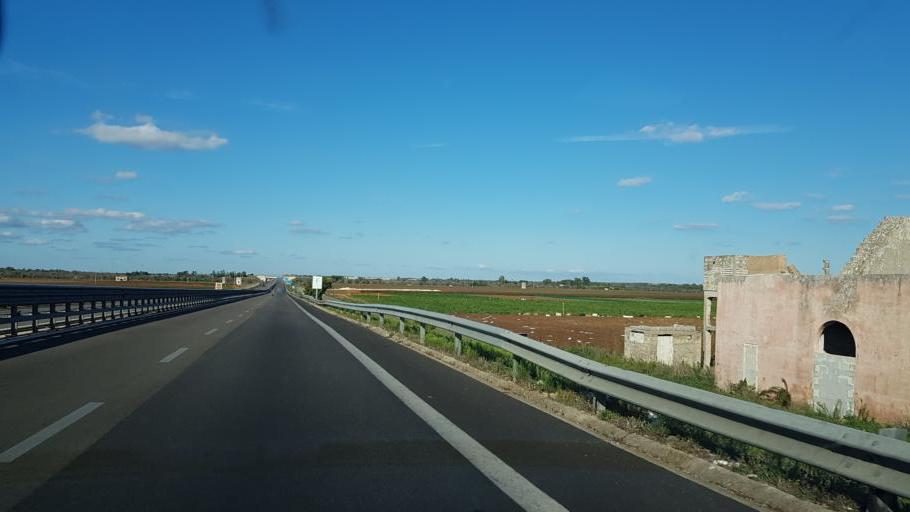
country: IT
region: Apulia
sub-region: Provincia di Lecce
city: Collemeto
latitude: 40.2489
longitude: 18.1148
